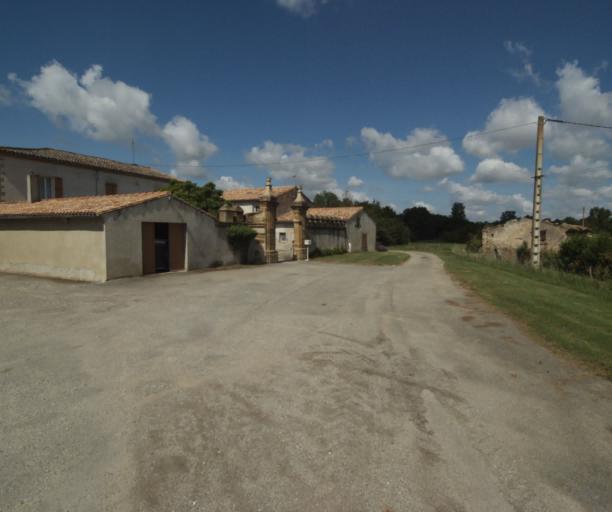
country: FR
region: Midi-Pyrenees
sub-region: Departement de la Haute-Garonne
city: Saint-Felix-Lauragais
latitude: 43.4280
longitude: 1.9417
